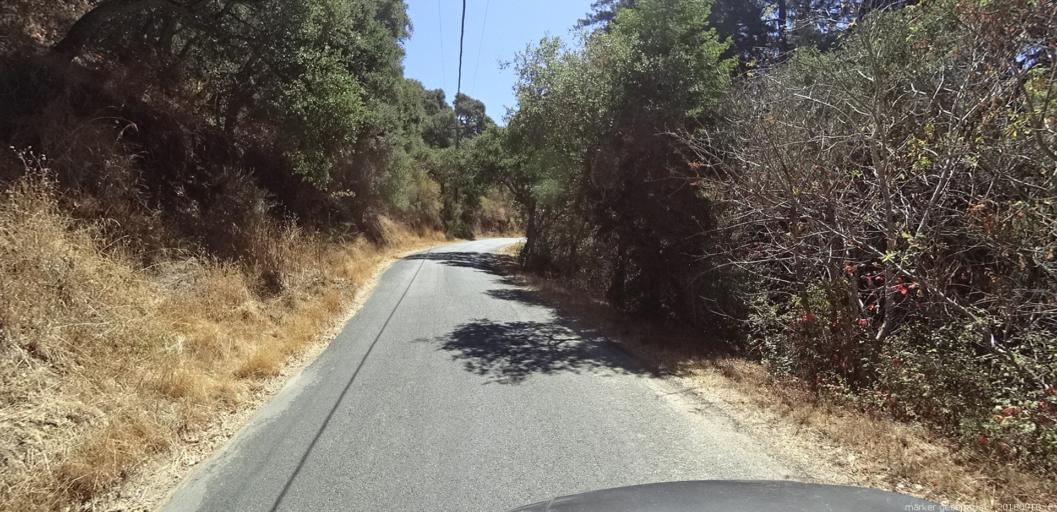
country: US
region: California
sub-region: Monterey County
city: Carmel Valley Village
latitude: 36.5116
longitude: -121.8111
